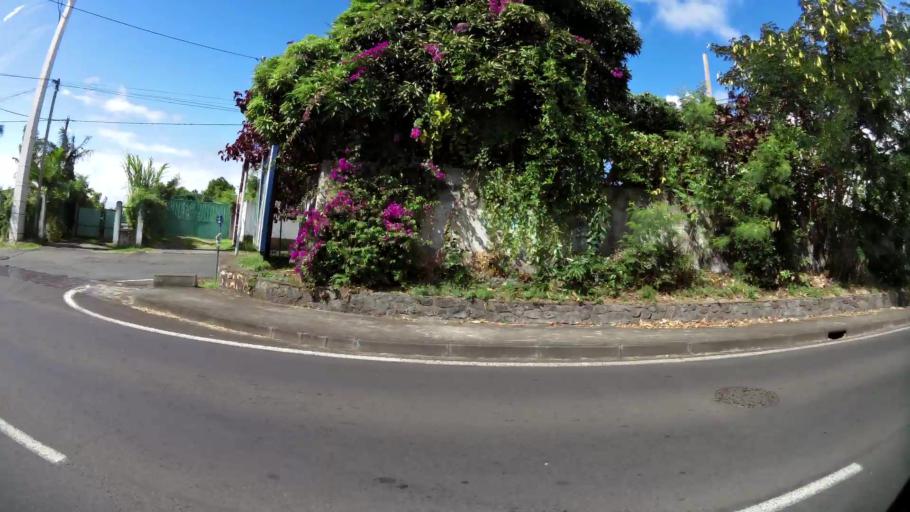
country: RE
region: Reunion
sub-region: Reunion
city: Sainte-Marie
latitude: -20.9129
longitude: 55.4978
